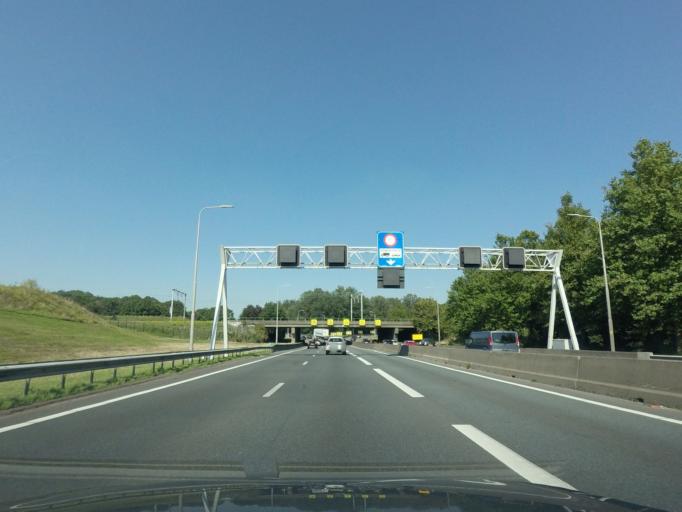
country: NL
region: South Holland
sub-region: Gemeente Rotterdam
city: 's-Gravenland
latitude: 51.9481
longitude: 4.5319
